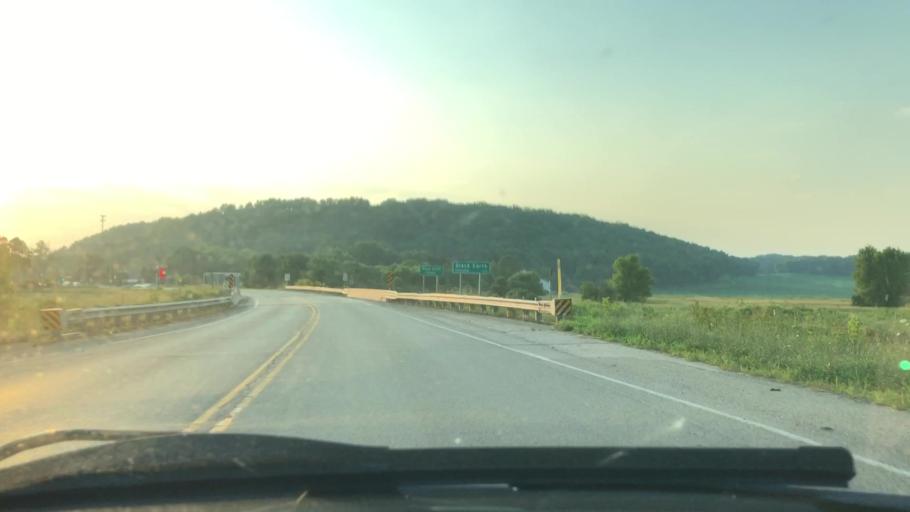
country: US
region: Wisconsin
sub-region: Dane County
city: Black Earth
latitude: 43.1412
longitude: -89.7427
